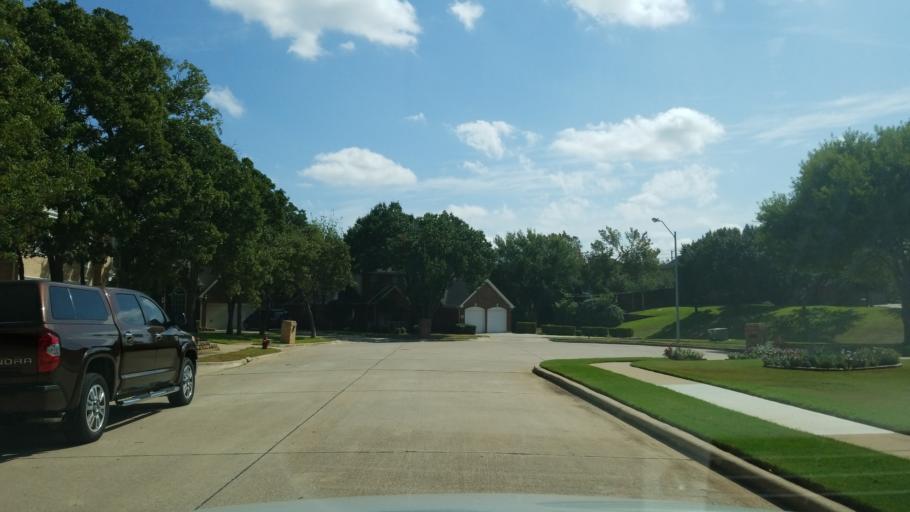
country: US
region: Texas
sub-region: Tarrant County
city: Euless
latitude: 32.8607
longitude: -97.1015
